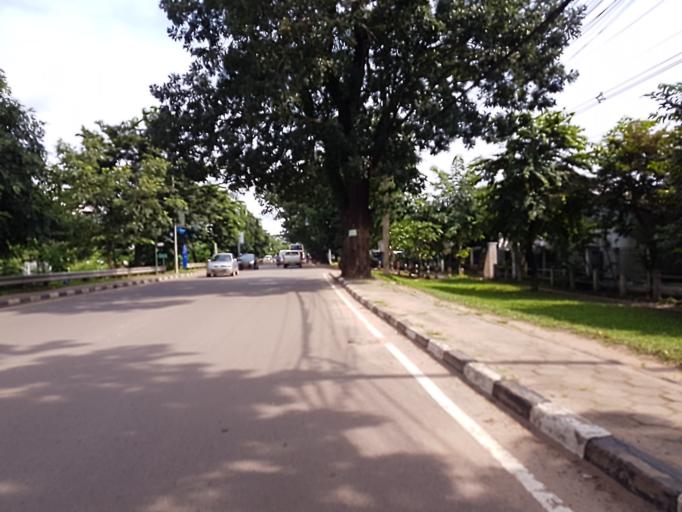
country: LA
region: Vientiane
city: Vientiane
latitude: 17.9581
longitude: 102.6206
